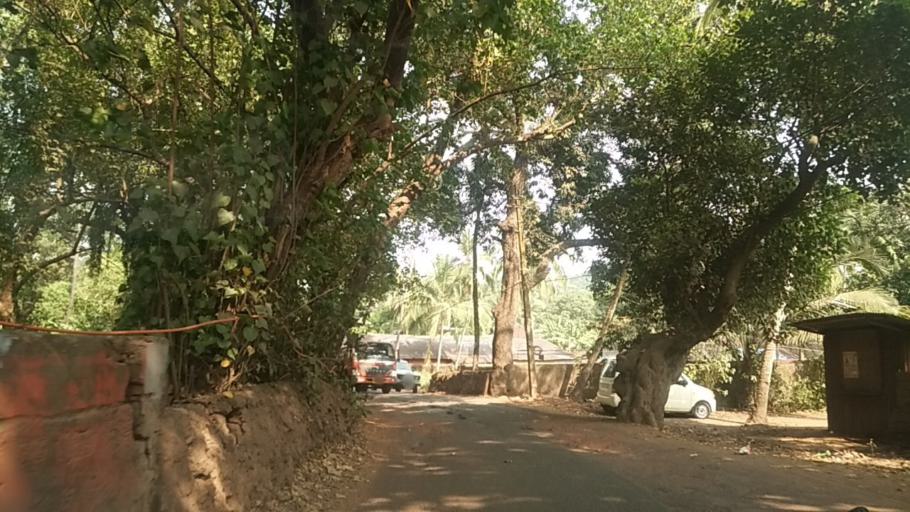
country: IN
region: Goa
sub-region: North Goa
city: Panaji
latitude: 15.5068
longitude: 73.8297
